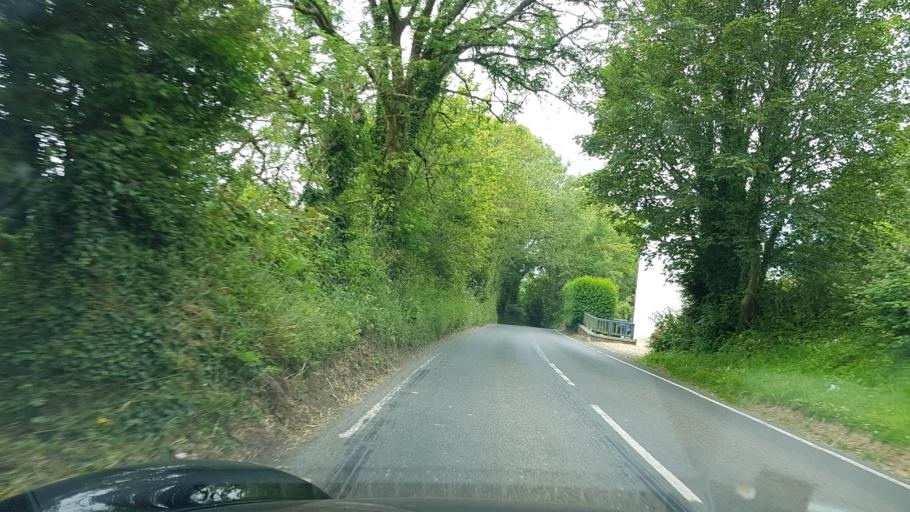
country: GB
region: Wales
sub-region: Pembrokeshire
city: Johnston
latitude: 51.7871
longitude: -5.0193
